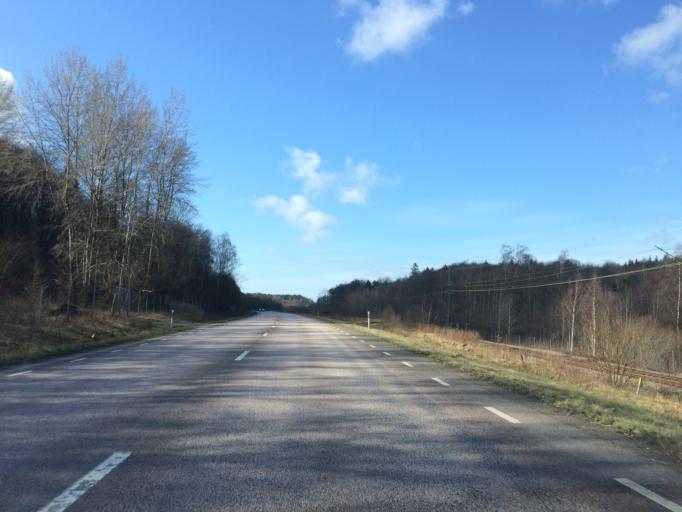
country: SE
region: Halland
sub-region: Laholms Kommun
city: Knared
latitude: 56.5172
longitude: 13.3025
